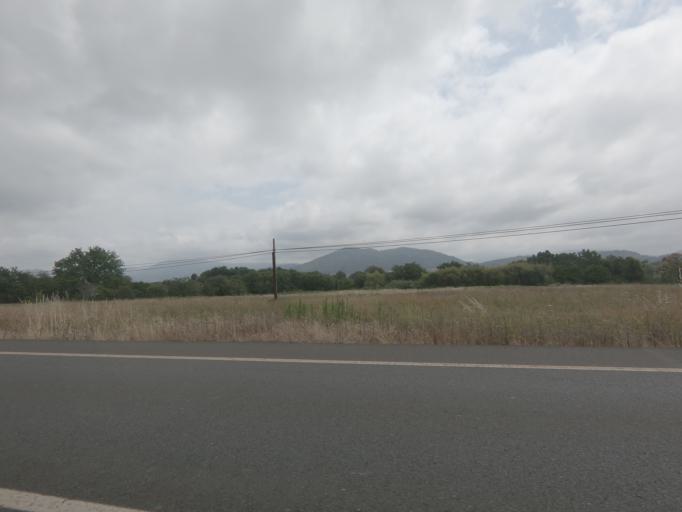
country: ES
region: Galicia
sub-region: Provincia de Pontevedra
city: O Rosal
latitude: 41.9207
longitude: -8.8119
